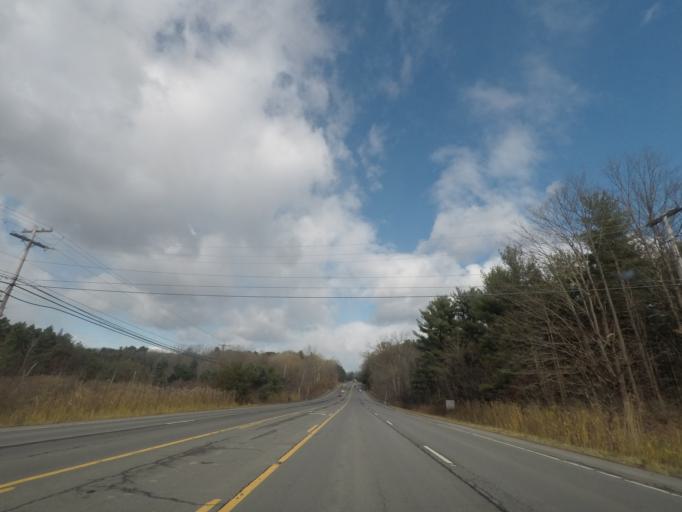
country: US
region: New York
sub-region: Saratoga County
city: Ballston Spa
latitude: 43.0055
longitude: -73.7902
